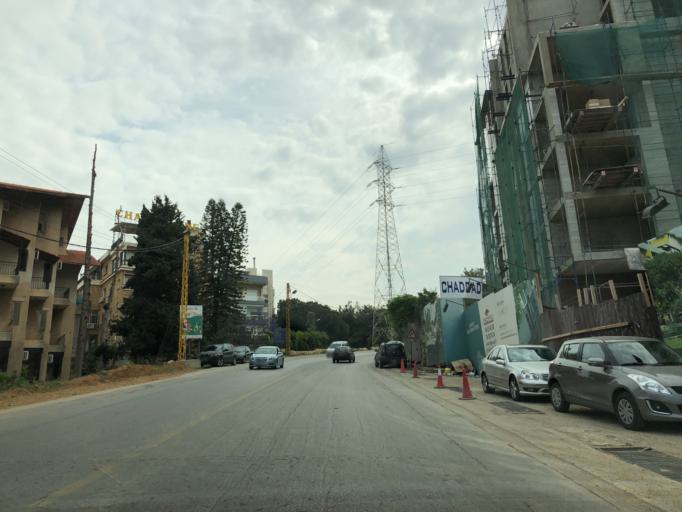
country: LB
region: Mont-Liban
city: Jdaidet el Matn
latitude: 33.8561
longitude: 35.5815
